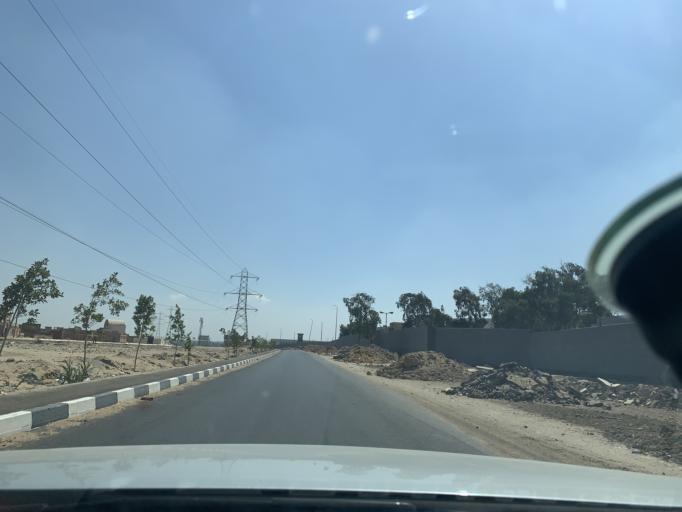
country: EG
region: Muhafazat al Qahirah
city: Cairo
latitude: 30.0297
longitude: 31.3488
